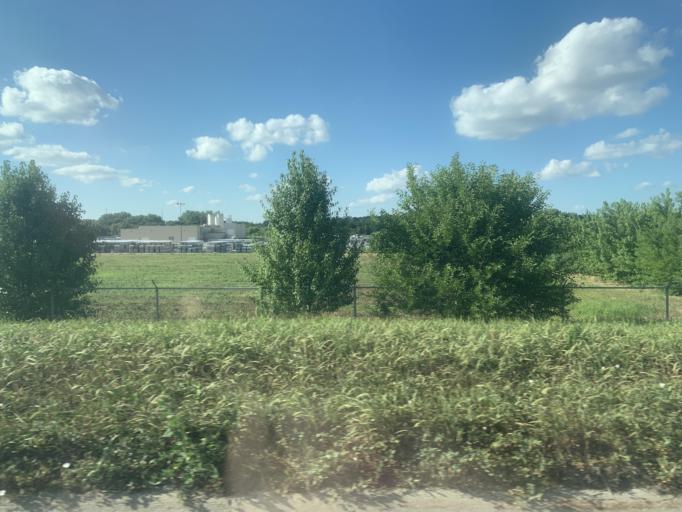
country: US
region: Nebraska
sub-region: Sarpy County
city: Chalco
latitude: 41.1763
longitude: -96.1353
